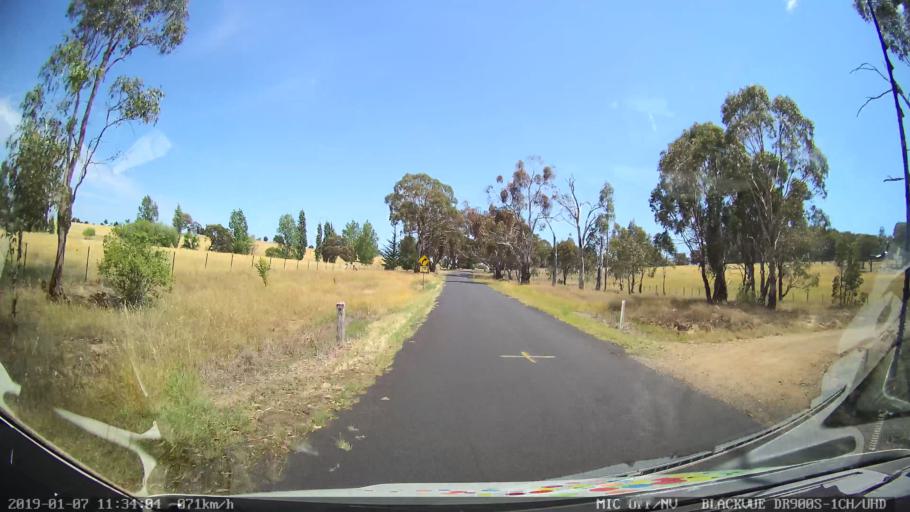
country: AU
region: New South Wales
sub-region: Armidale Dumaresq
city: Armidale
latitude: -30.3934
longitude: 151.5602
